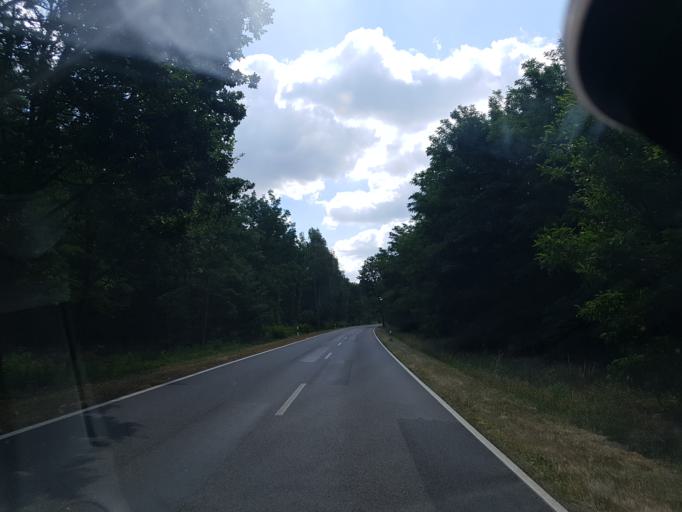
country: DE
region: Brandenburg
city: Neupetershain
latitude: 51.6827
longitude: 14.1490
